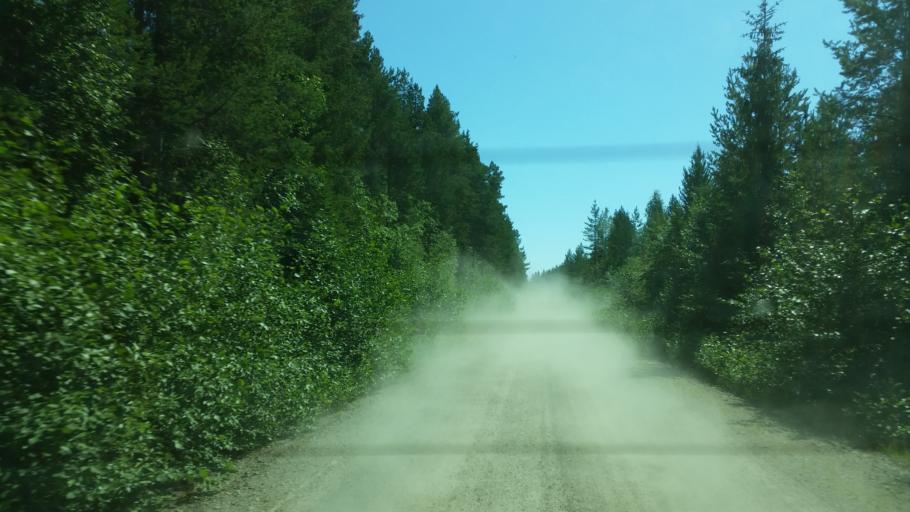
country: SE
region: Vaesternorrland
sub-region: Ange Kommun
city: Ange
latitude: 62.1878
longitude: 15.5990
